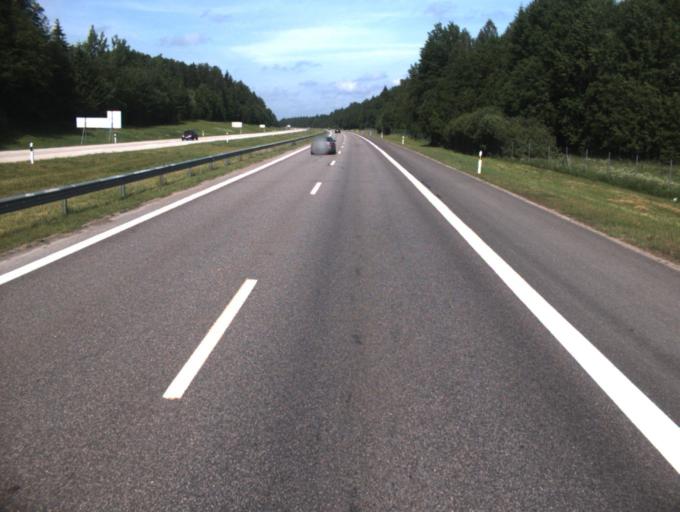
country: LT
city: Rietavas
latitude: 55.6894
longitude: 21.6854
